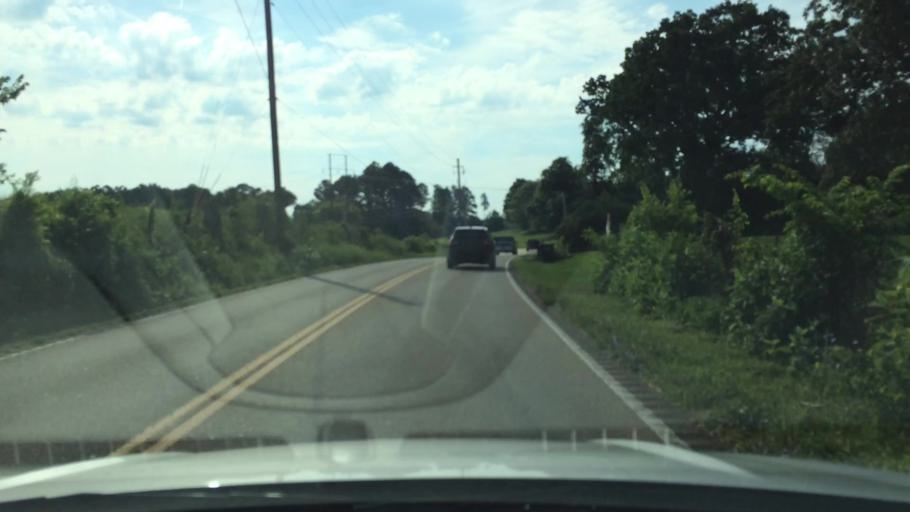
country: US
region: Tennessee
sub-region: Sevier County
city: Sevierville
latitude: 35.9234
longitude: -83.5970
